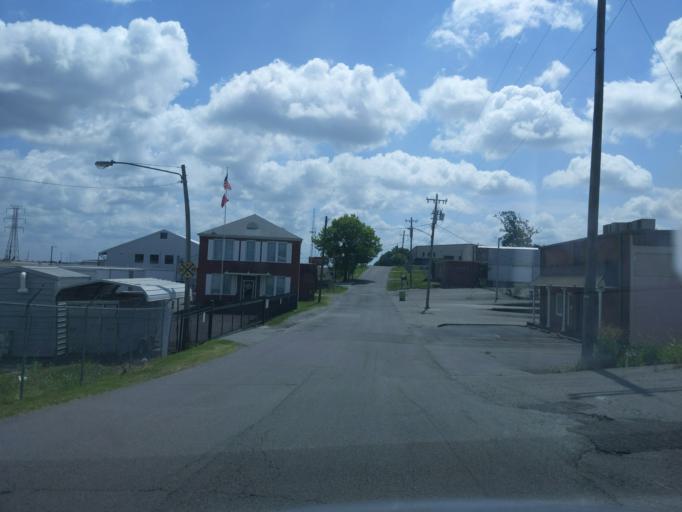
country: US
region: Tennessee
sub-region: Davidson County
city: Nashville
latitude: 36.1549
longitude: -86.7552
